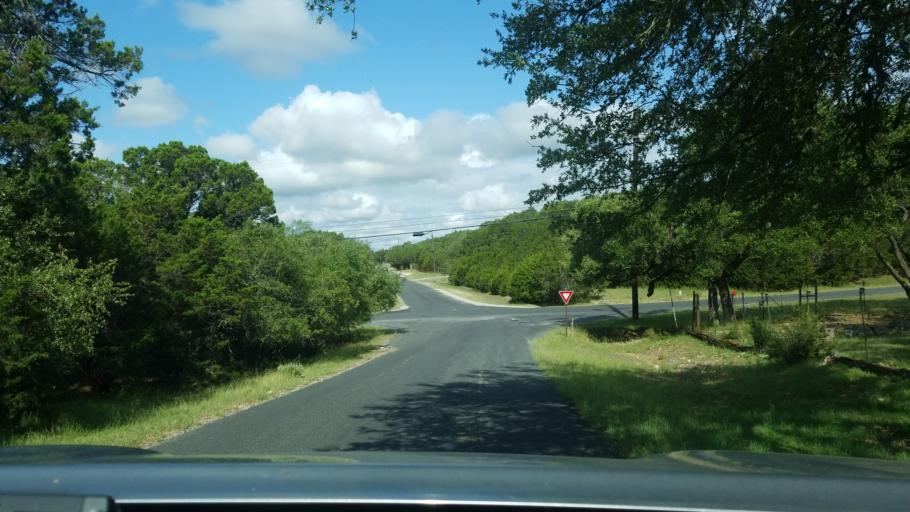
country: US
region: Texas
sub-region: Comal County
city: Bulverde
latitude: 29.7656
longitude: -98.4456
